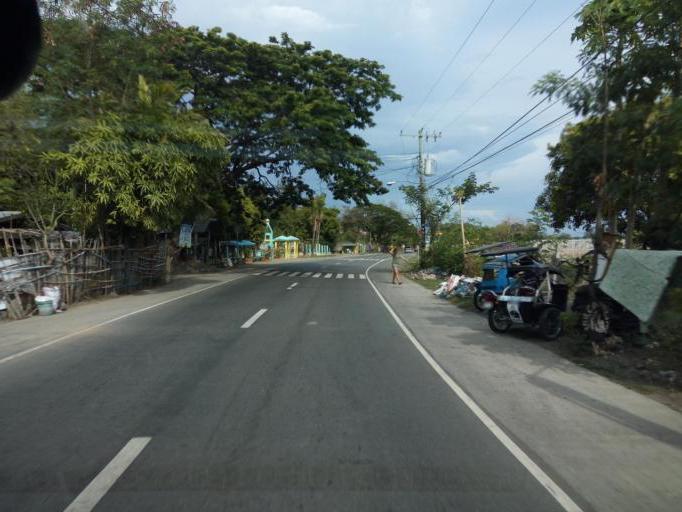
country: PH
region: Central Luzon
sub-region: Province of Nueva Ecija
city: Sibul
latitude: 15.8117
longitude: 120.9650
